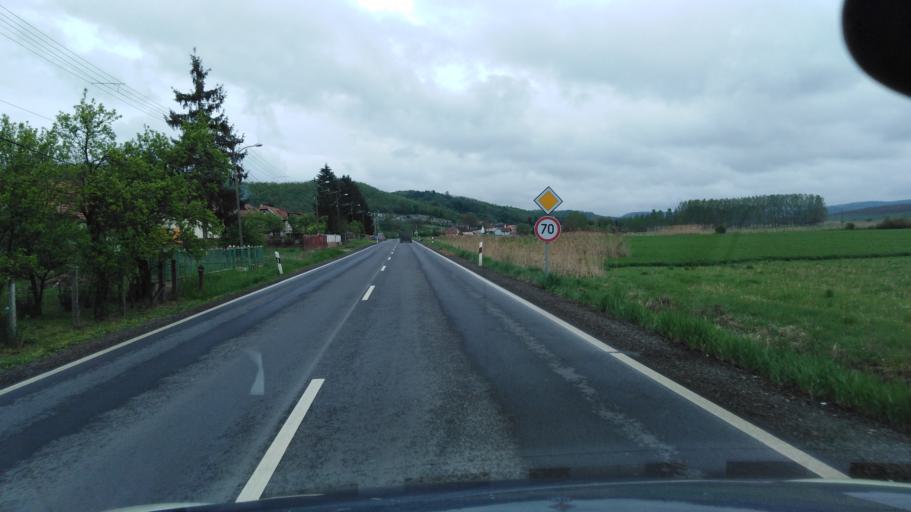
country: HU
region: Nograd
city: Karancskeszi
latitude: 48.1109
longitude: 19.6697
